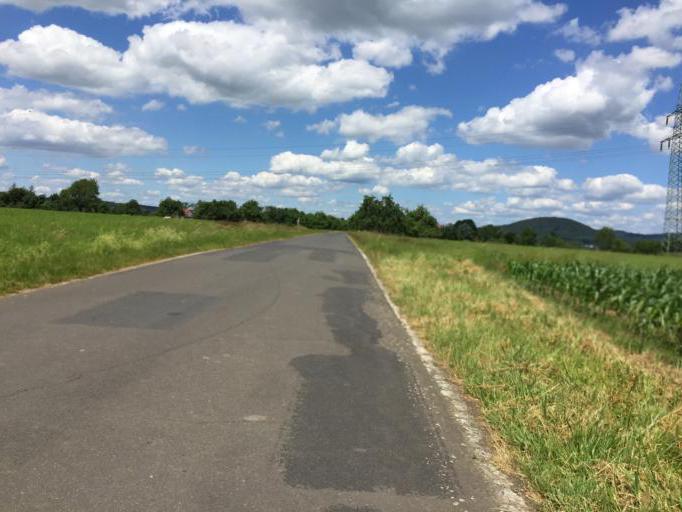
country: DE
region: Rheinland-Pfalz
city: Bannberscheid
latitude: 50.4595
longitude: 7.8283
